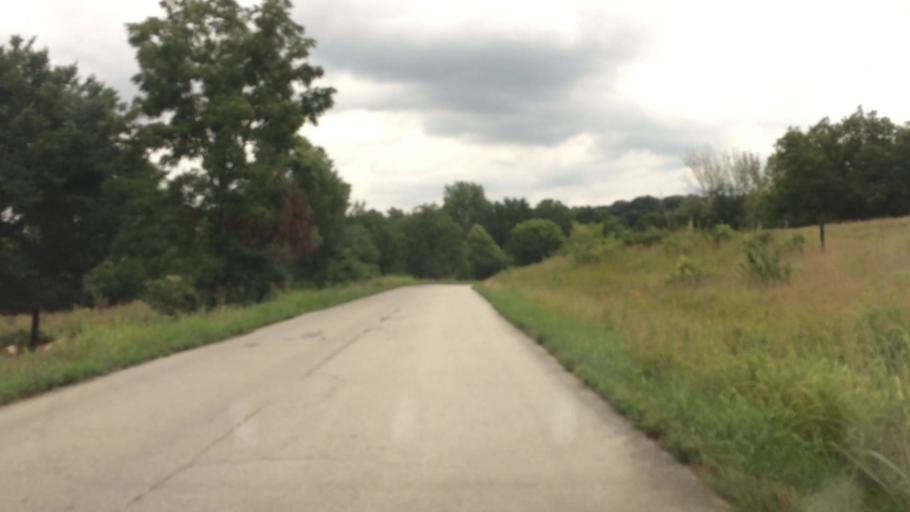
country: US
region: Missouri
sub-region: Greene County
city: Strafford
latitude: 37.3068
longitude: -93.0727
